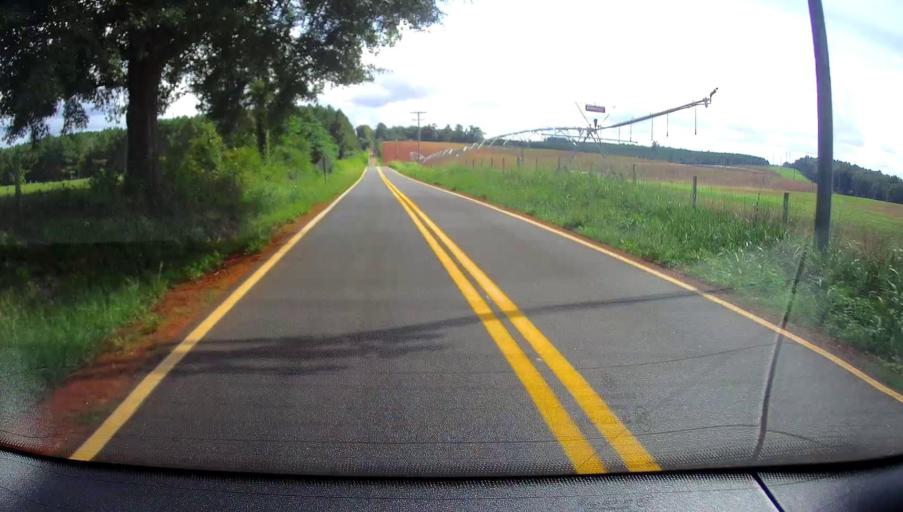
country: US
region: Georgia
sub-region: Upson County
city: Hannahs Mill
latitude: 32.9443
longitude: -84.2903
